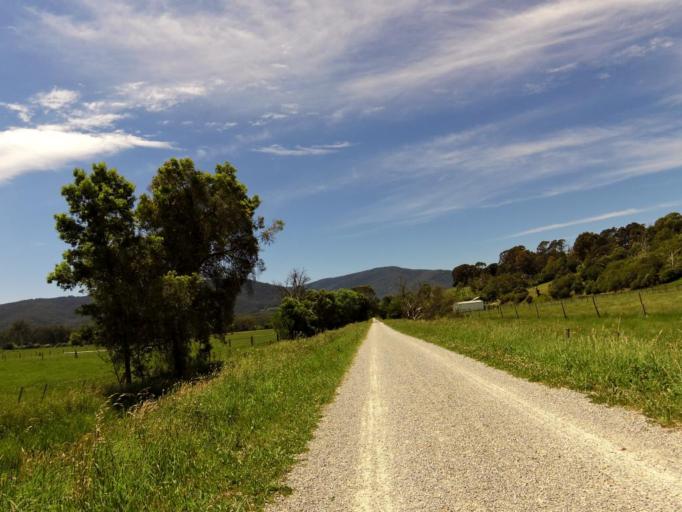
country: AU
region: Victoria
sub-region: Yarra Ranges
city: Woori Yallock
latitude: -37.7696
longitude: 145.5408
